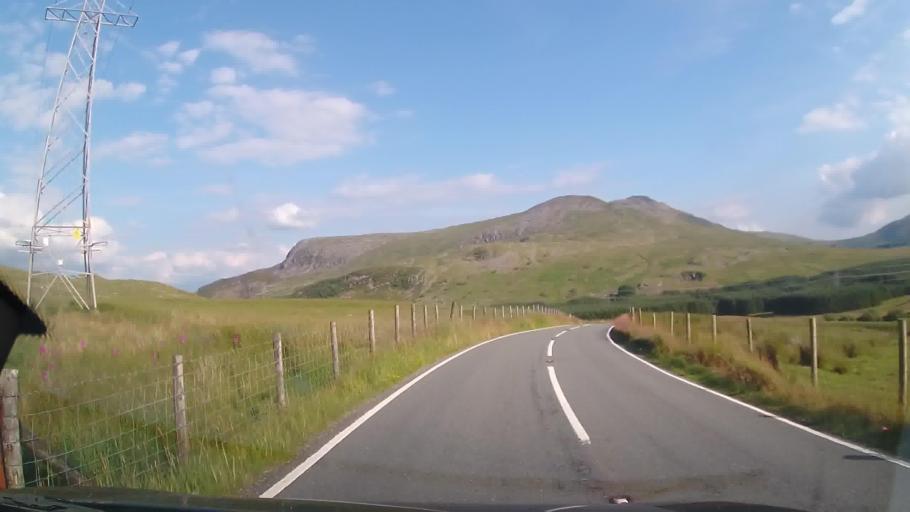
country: GB
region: Wales
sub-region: Conwy
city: Betws-y-Coed
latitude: 52.9413
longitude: -3.7693
